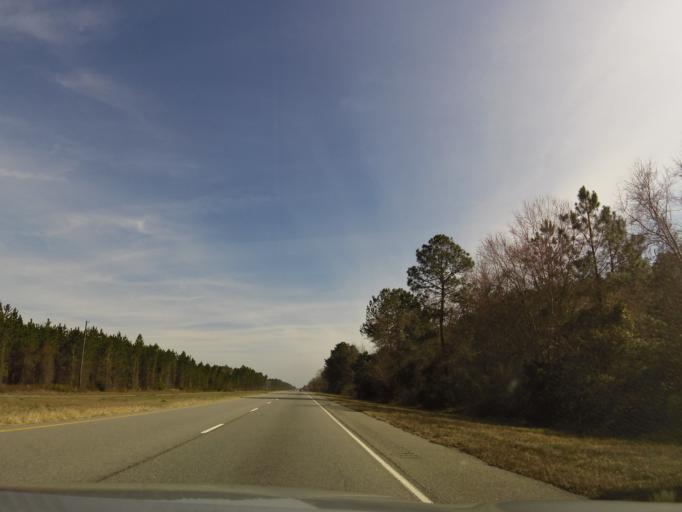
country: US
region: Georgia
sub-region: Lanier County
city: Lakeland
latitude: 30.9578
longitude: -82.9508
